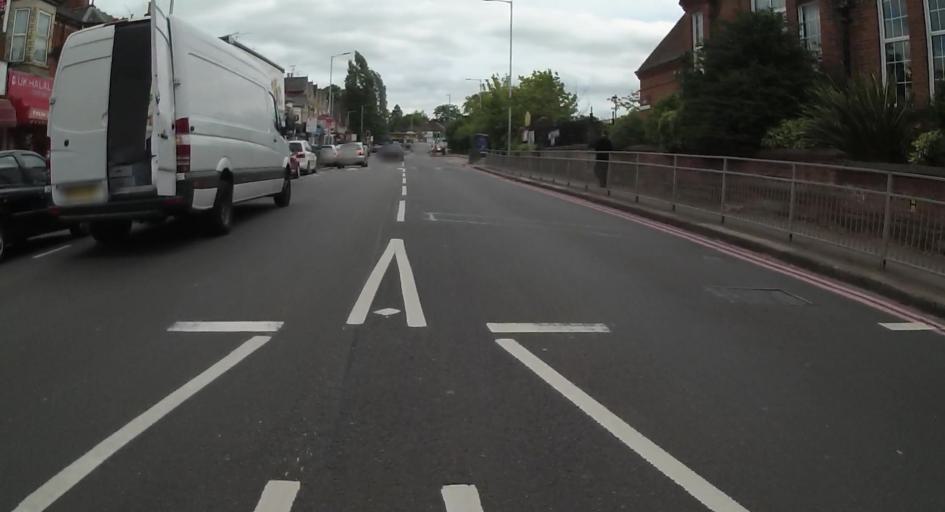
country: GB
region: England
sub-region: Wokingham
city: Earley
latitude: 51.4488
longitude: -0.9374
